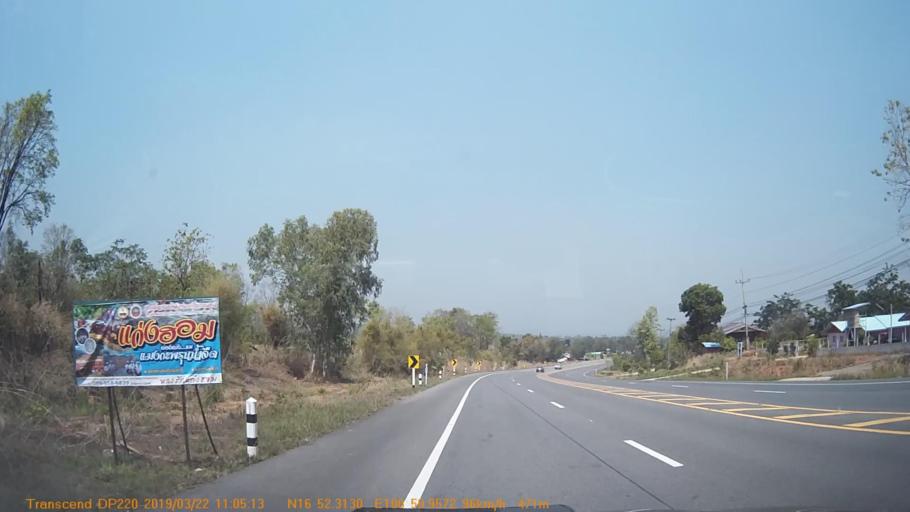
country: TH
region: Phitsanulok
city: Nakhon Thai
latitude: 16.8720
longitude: 100.8489
